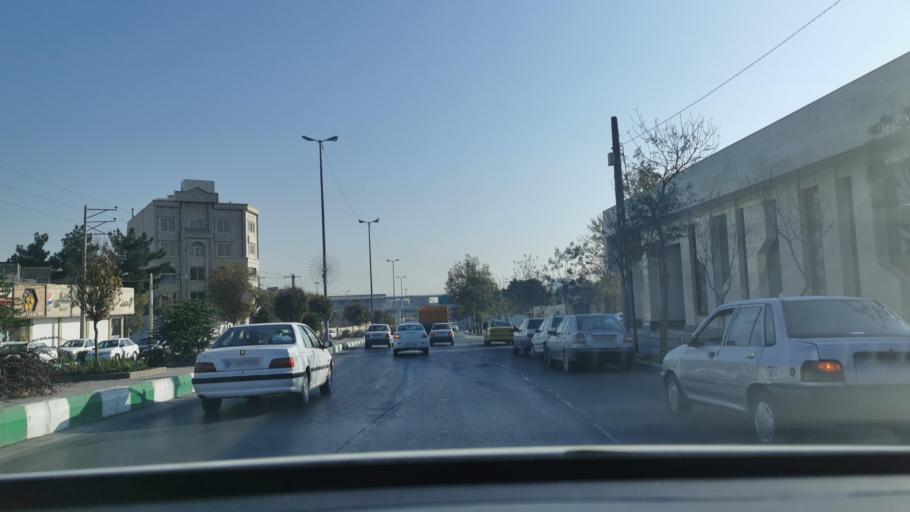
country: IR
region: Razavi Khorasan
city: Mashhad
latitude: 36.2846
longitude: 59.5505
